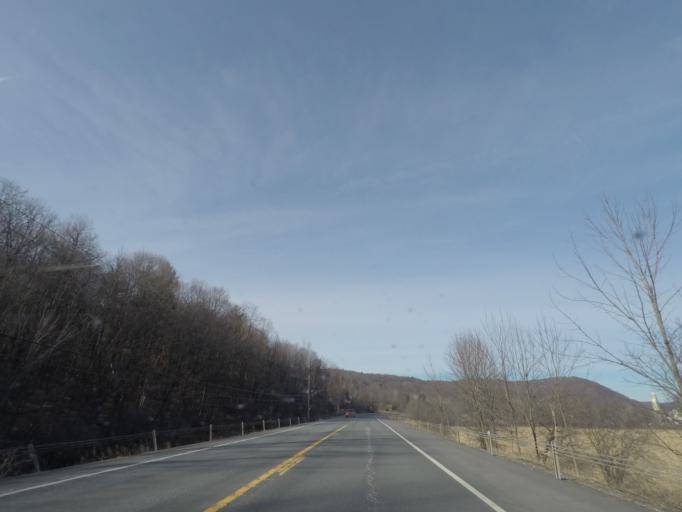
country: US
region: Massachusetts
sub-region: Berkshire County
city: Williamstown
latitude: 42.7071
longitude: -73.3781
